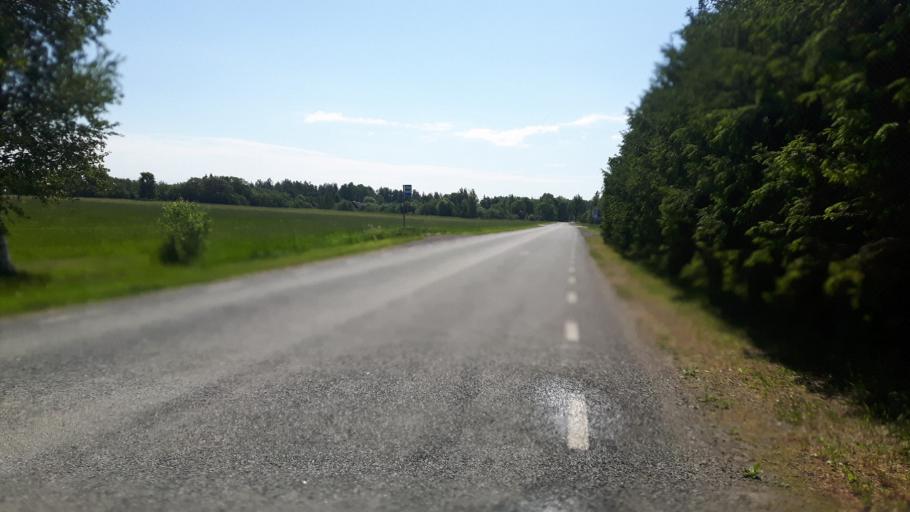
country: EE
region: Paernumaa
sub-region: Vaendra vald (alev)
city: Vandra
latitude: 58.5948
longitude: 25.0243
